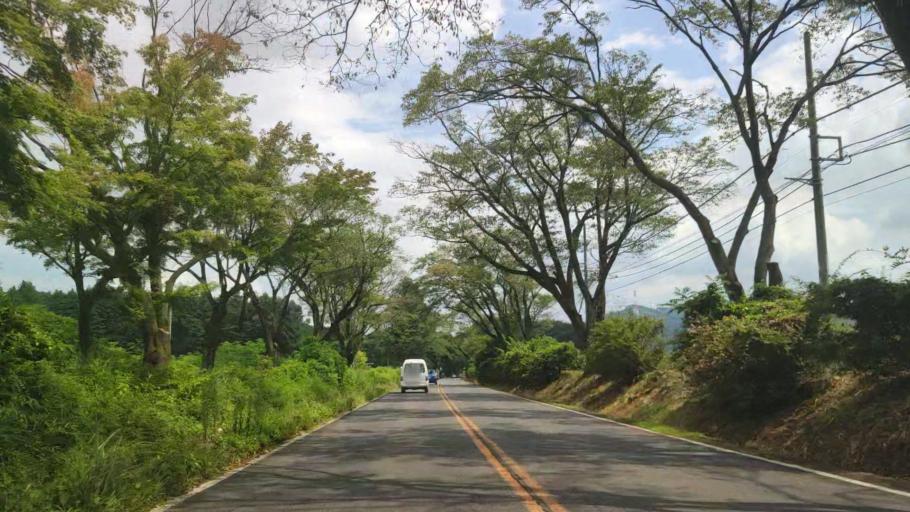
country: JP
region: Tochigi
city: Imaichi
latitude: 36.6786
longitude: 139.7970
